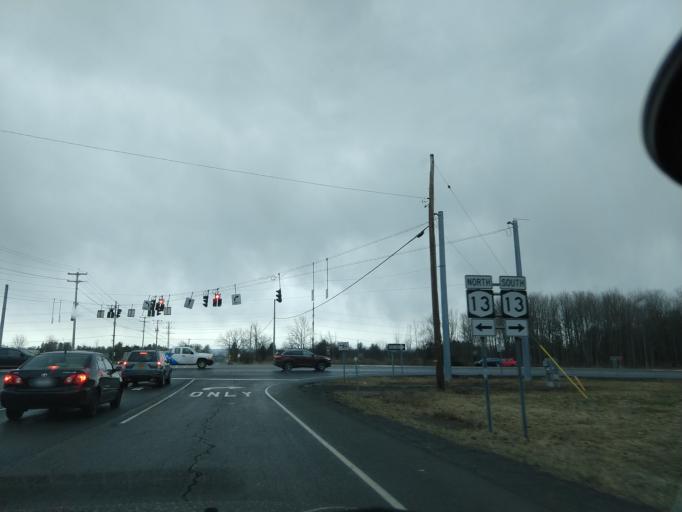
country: US
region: New York
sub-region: Tompkins County
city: Lansing
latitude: 42.4828
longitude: -76.4674
